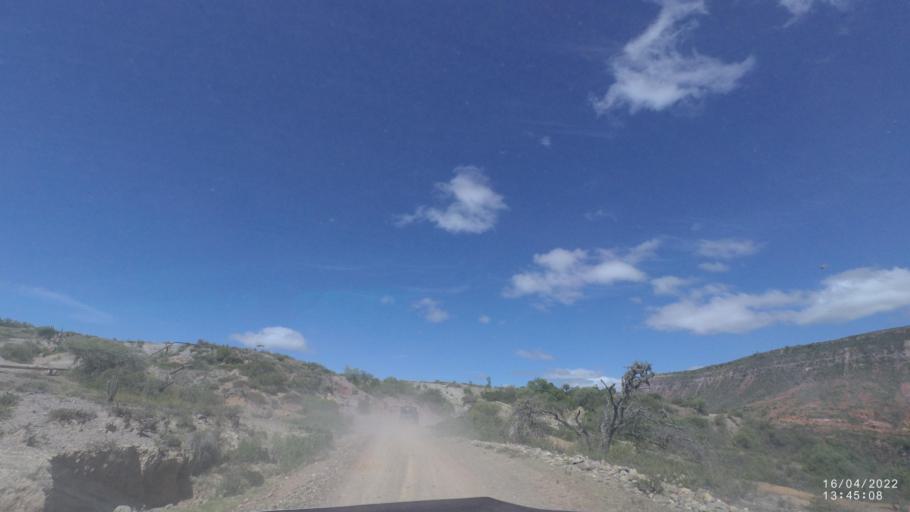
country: BO
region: Cochabamba
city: Mizque
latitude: -18.0020
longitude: -65.5922
